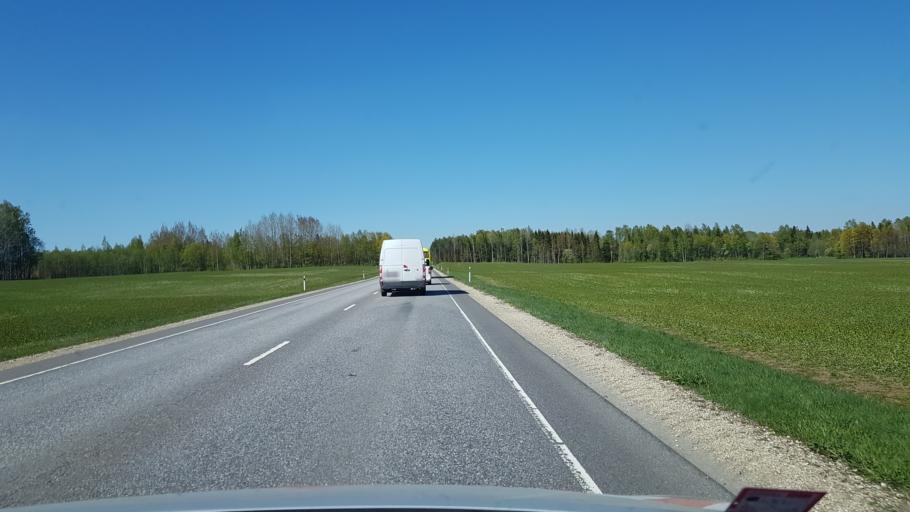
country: EE
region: Vorumaa
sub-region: Antsla vald
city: Vana-Antsla
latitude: 58.0463
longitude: 26.7297
